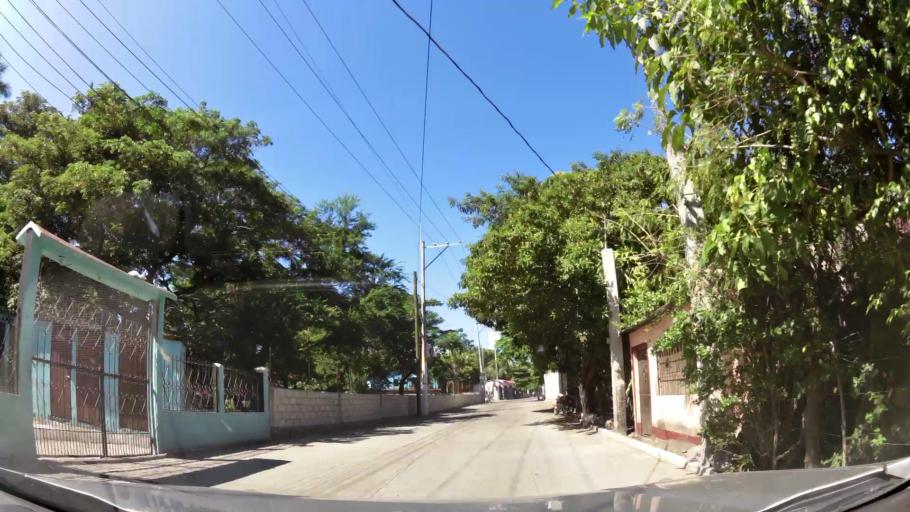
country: GT
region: Escuintla
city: Iztapa
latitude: 13.9390
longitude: -90.7080
